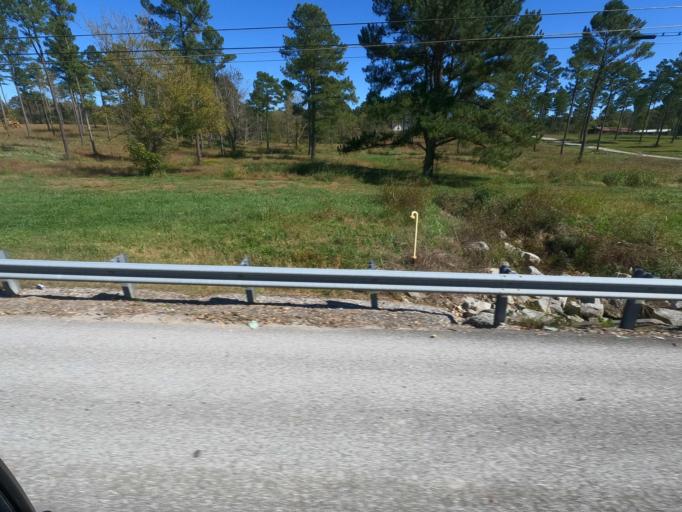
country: US
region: Tennessee
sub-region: Maury County
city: Mount Pleasant
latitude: 35.3924
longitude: -87.2770
